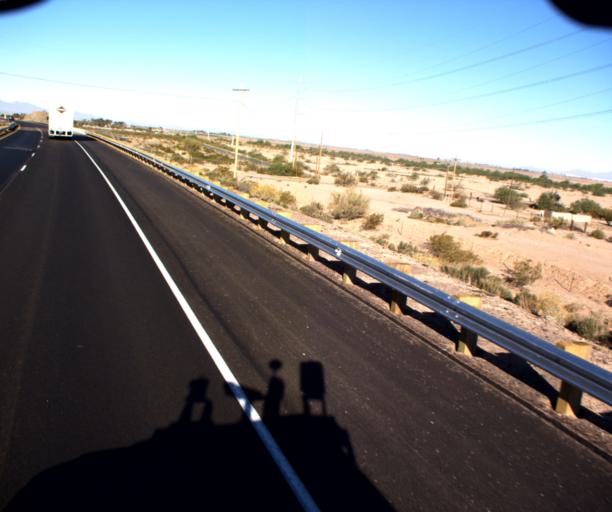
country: US
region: Arizona
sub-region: Pinal County
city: Casa Grande
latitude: 32.8353
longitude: -111.7214
